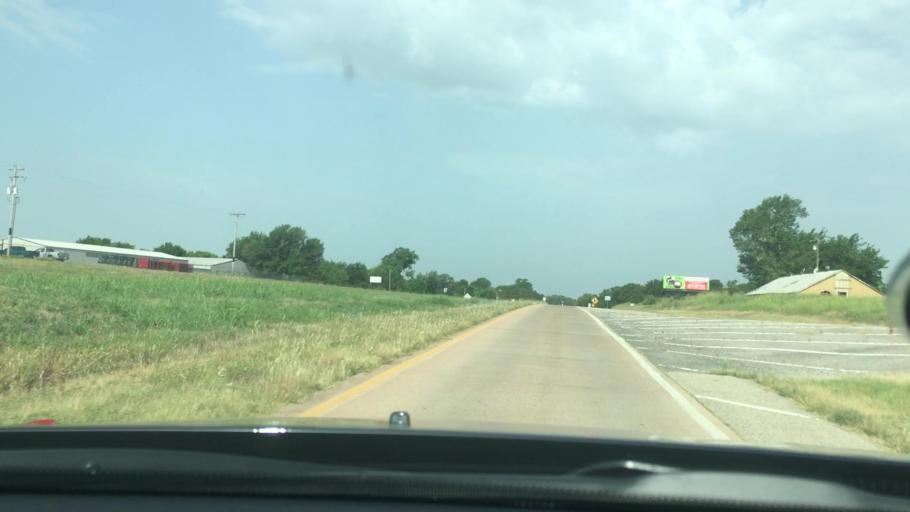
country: US
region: Oklahoma
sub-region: Pontotoc County
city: Ada
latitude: 34.7857
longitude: -96.7263
